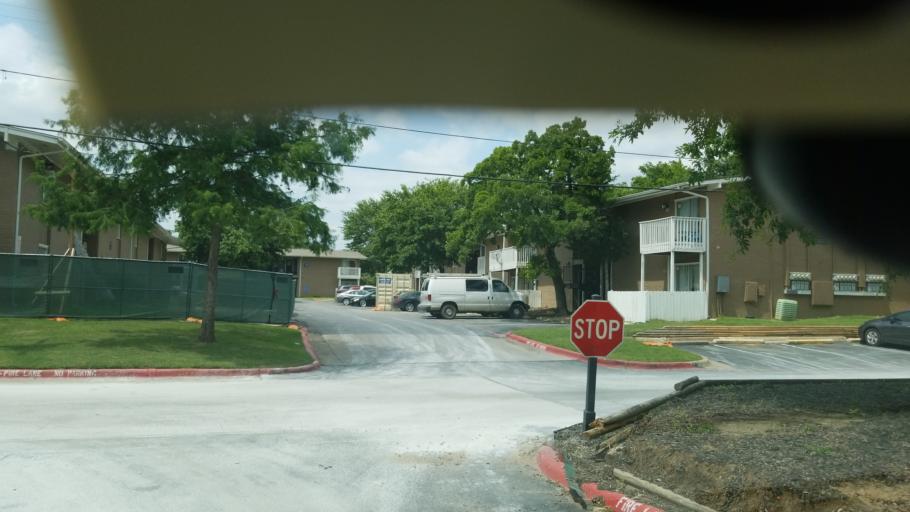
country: US
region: Texas
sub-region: Dallas County
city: Irving
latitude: 32.8401
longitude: -96.9578
